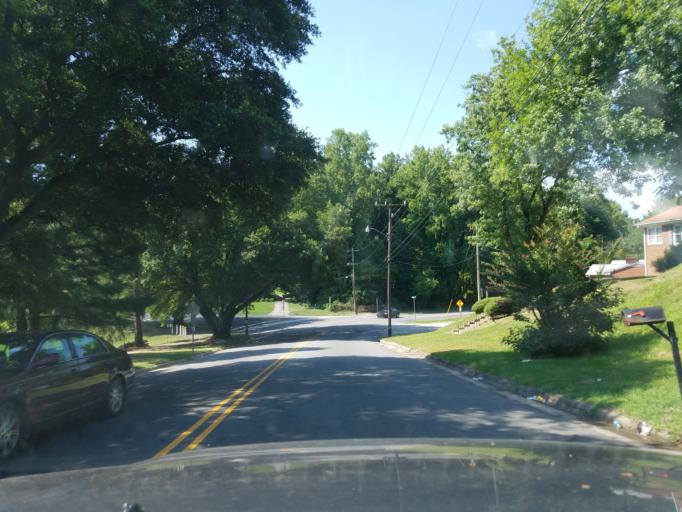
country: US
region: North Carolina
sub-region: Durham County
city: Durham
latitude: 35.9775
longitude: -78.9067
